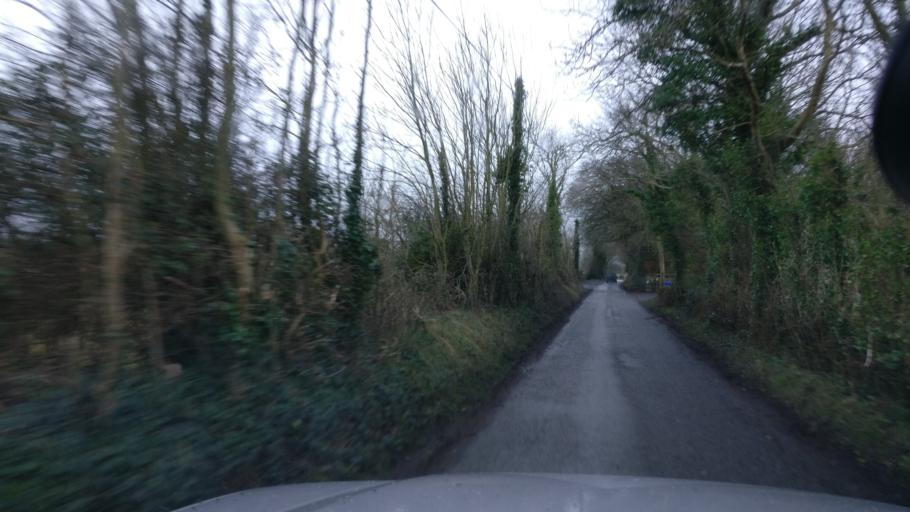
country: IE
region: Connaught
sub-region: County Galway
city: Loughrea
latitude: 53.1965
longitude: -8.6632
